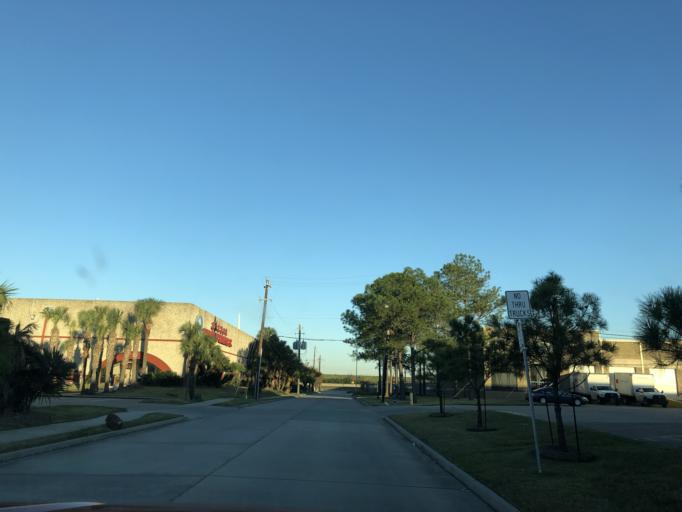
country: US
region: Texas
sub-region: Harris County
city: Jacinto City
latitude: 29.7585
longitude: -95.2682
